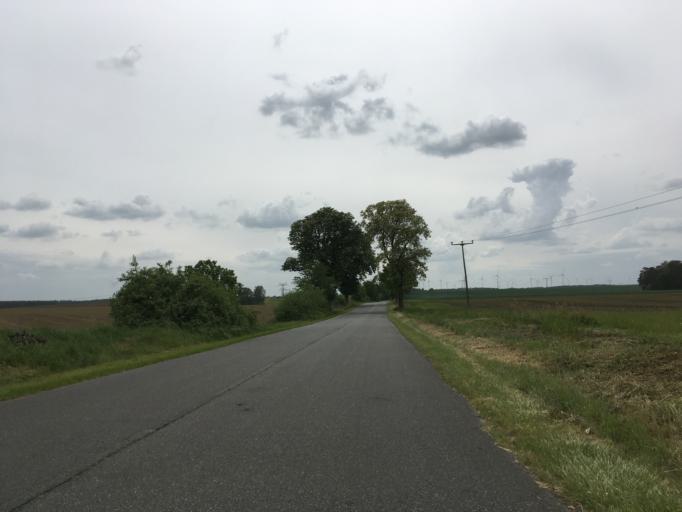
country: DE
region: Brandenburg
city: Melchow
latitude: 52.7302
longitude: 13.7529
